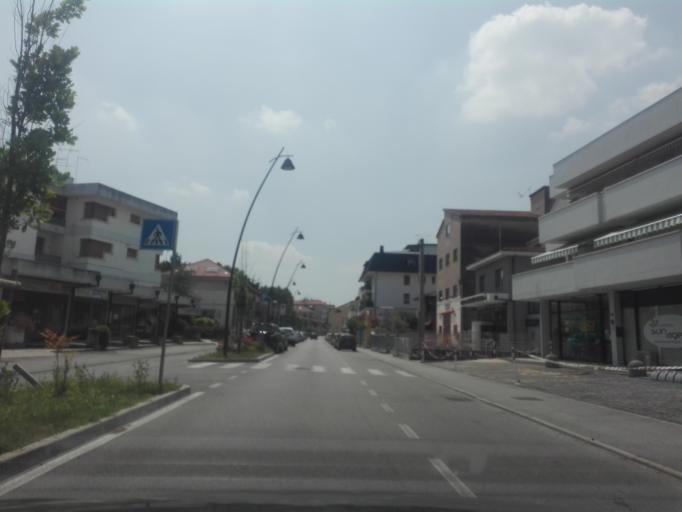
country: IT
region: Veneto
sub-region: Provincia di Rovigo
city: Rovigo
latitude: 45.0732
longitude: 11.7981
